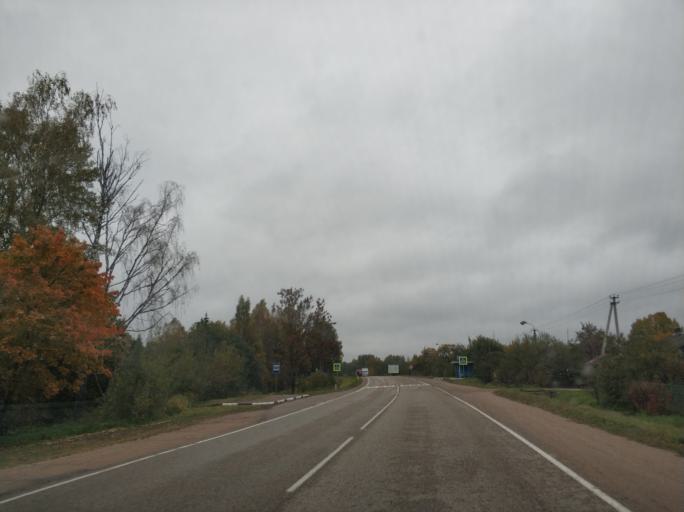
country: BY
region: Vitebsk
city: Rasony
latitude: 56.0559
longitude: 28.7129
